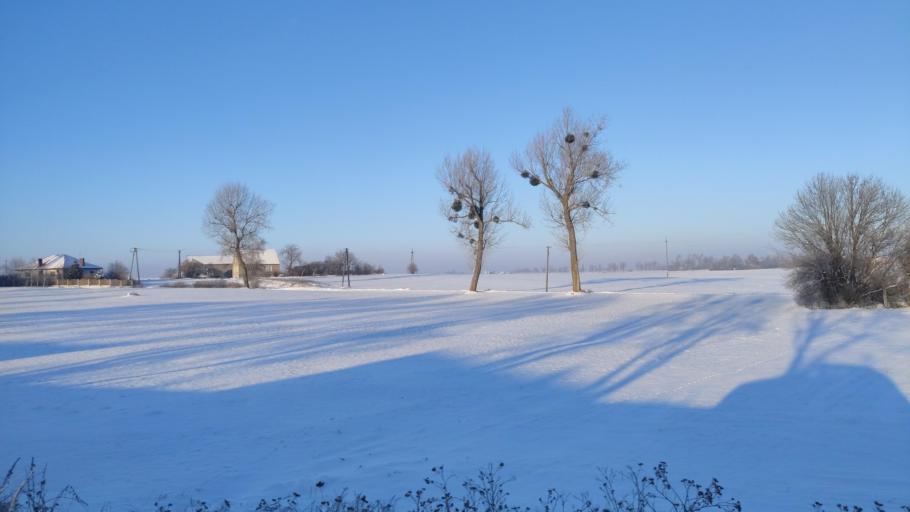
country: PL
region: Kujawsko-Pomorskie
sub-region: Powiat zninski
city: Znin
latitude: 52.8663
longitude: 17.7952
